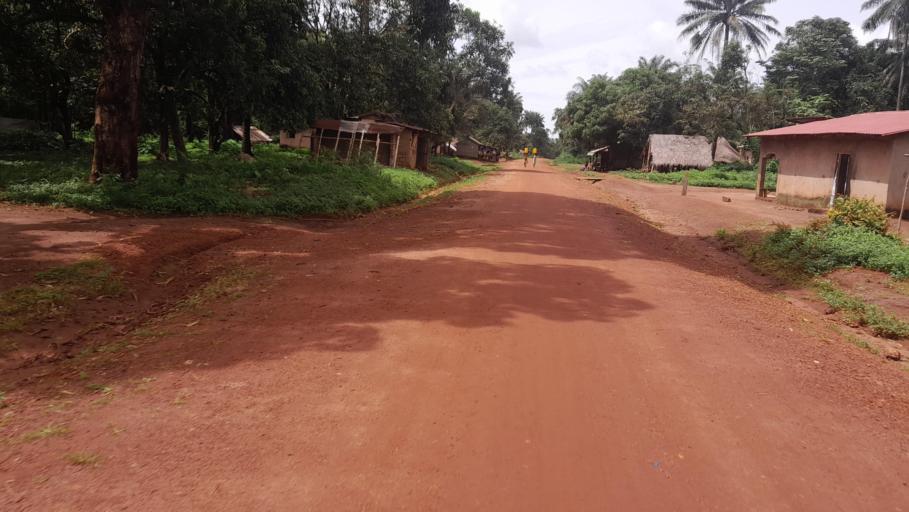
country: GN
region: Boke
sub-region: Boffa
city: Boffa
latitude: 10.0087
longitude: -13.8867
